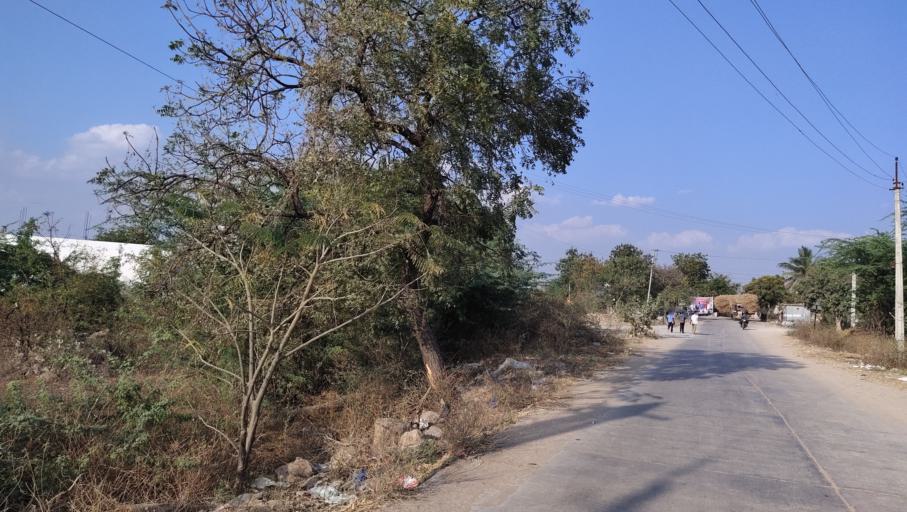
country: IN
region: Andhra Pradesh
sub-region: Anantapur
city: Tadpatri
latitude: 14.9397
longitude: 77.8678
